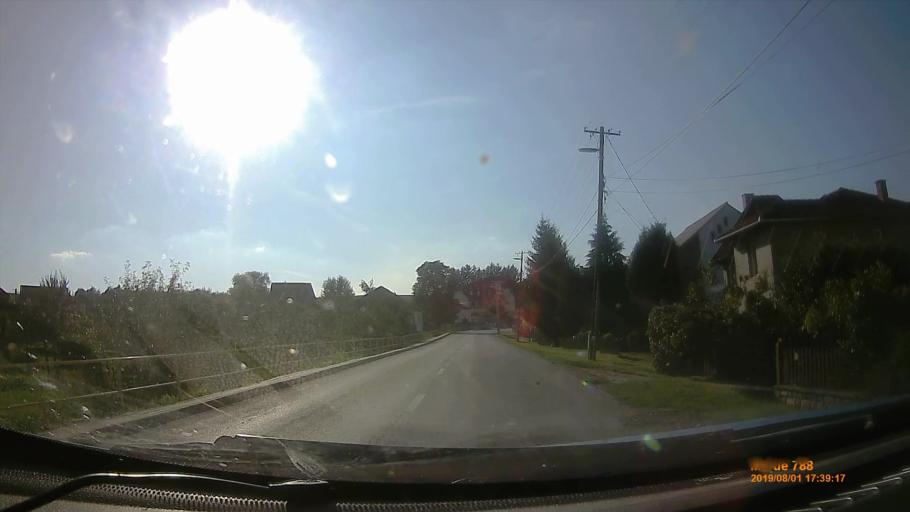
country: HU
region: Baranya
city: Komlo
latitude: 46.1967
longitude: 18.1934
